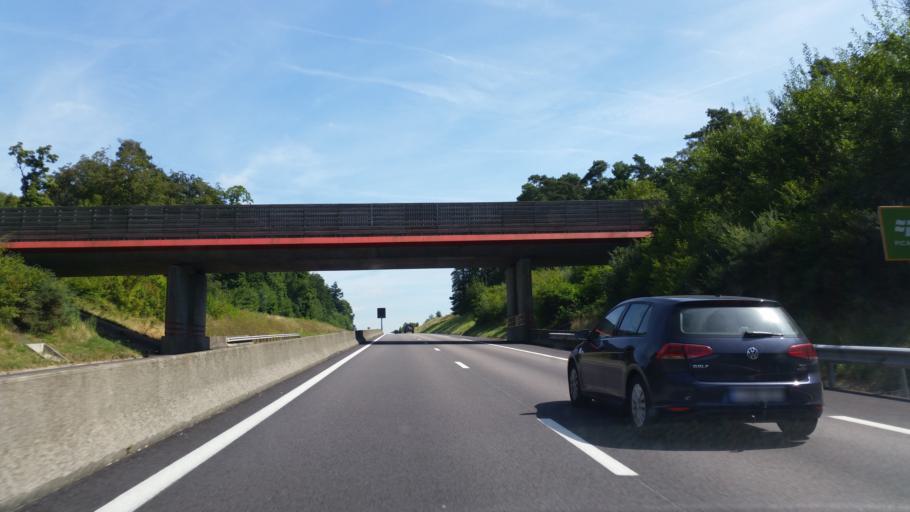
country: FR
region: Haute-Normandie
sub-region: Departement de la Seine-Maritime
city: Aumale
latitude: 49.7869
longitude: 1.7705
